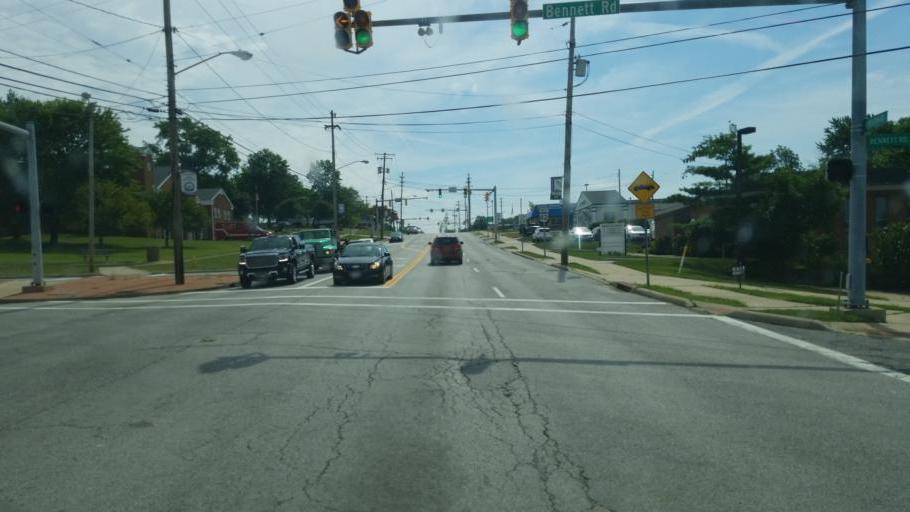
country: US
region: Ohio
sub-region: Cuyahoga County
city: North Royalton
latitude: 41.3137
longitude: -81.7375
